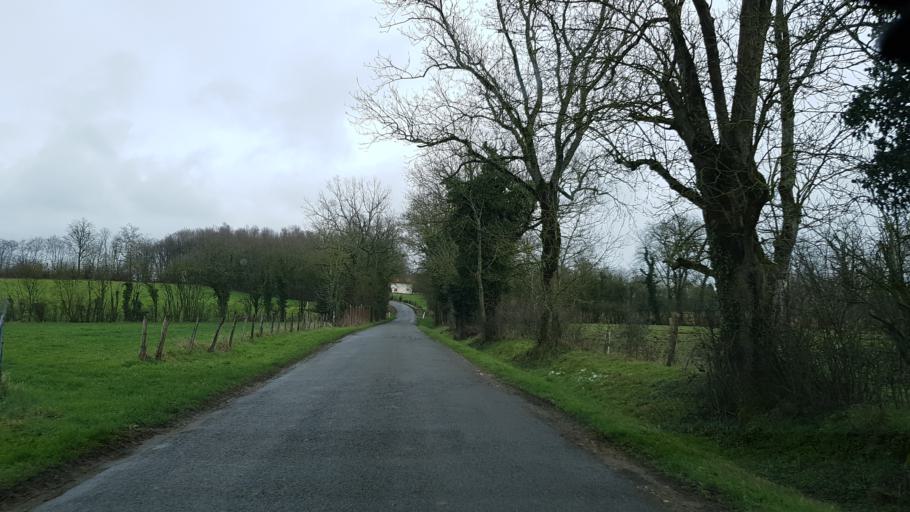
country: FR
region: Rhone-Alpes
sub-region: Departement de l'Ain
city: Saint-Denis-les-Bourg
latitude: 46.1851
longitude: 5.1789
